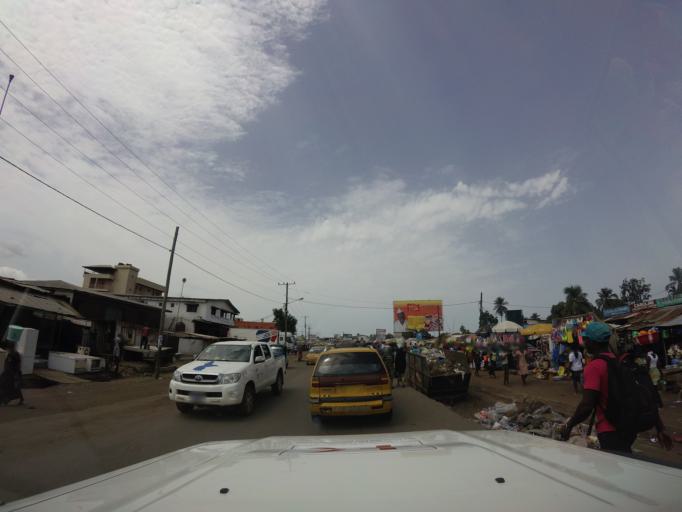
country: LR
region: Montserrado
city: Monrovia
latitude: 6.3752
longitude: -10.7862
